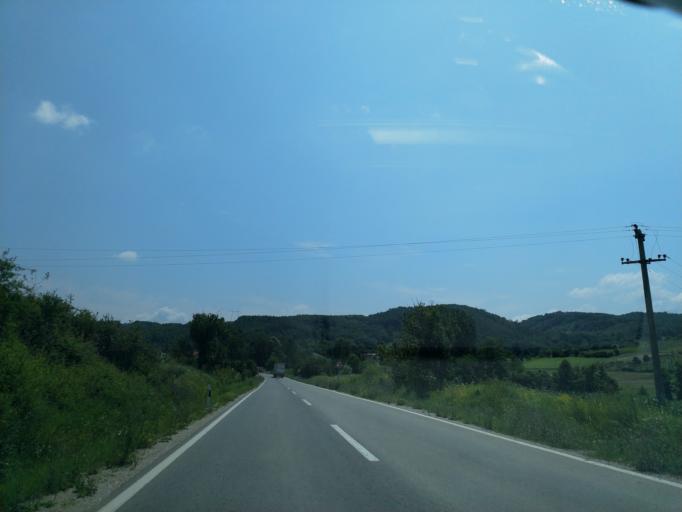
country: RS
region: Central Serbia
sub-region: Toplicki Okrug
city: Blace
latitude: 43.3092
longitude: 21.2477
